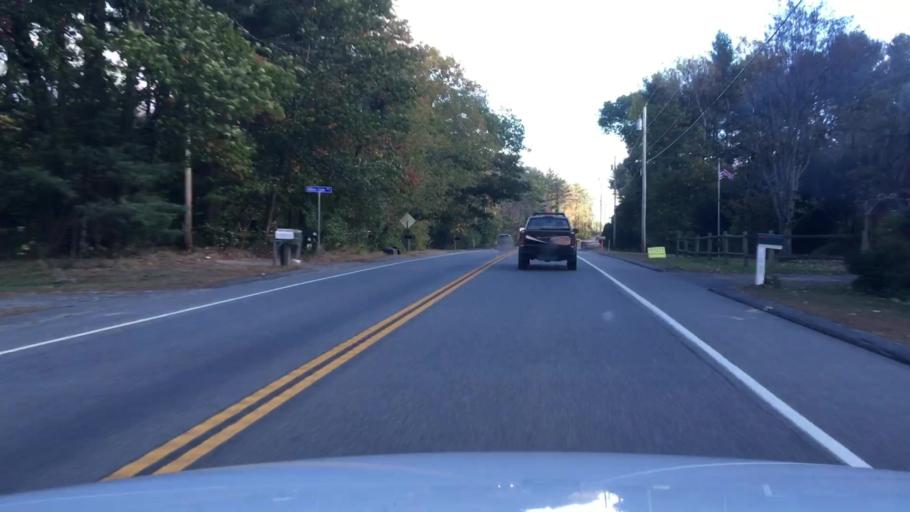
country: US
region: Maine
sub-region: York County
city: Wells Beach Station
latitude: 43.3367
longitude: -70.6328
